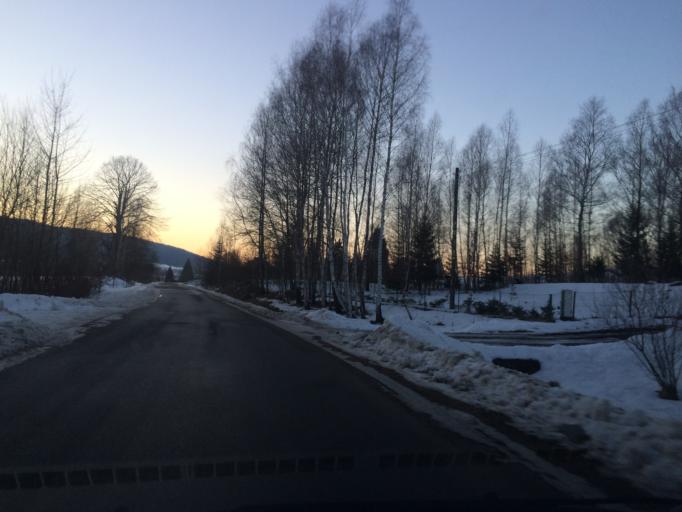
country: PL
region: Subcarpathian Voivodeship
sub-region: Powiat bieszczadzki
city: Ustrzyki Dolne
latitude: 49.3989
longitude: 22.6145
